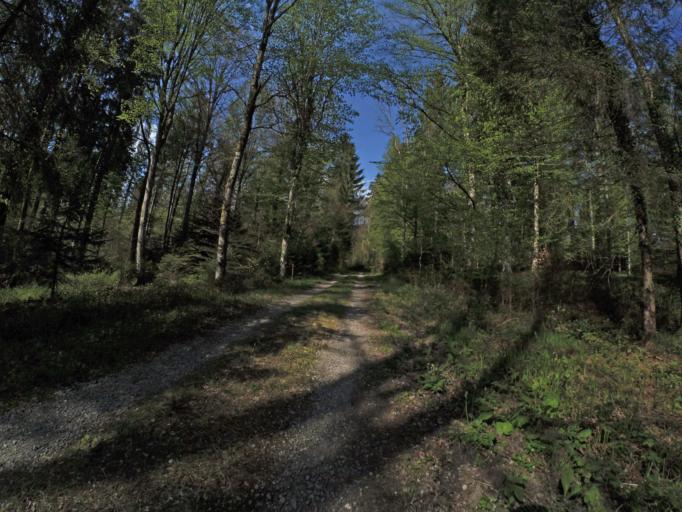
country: CH
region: Thurgau
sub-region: Frauenfeld District
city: Diessenhofen
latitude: 47.6492
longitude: 8.7475
